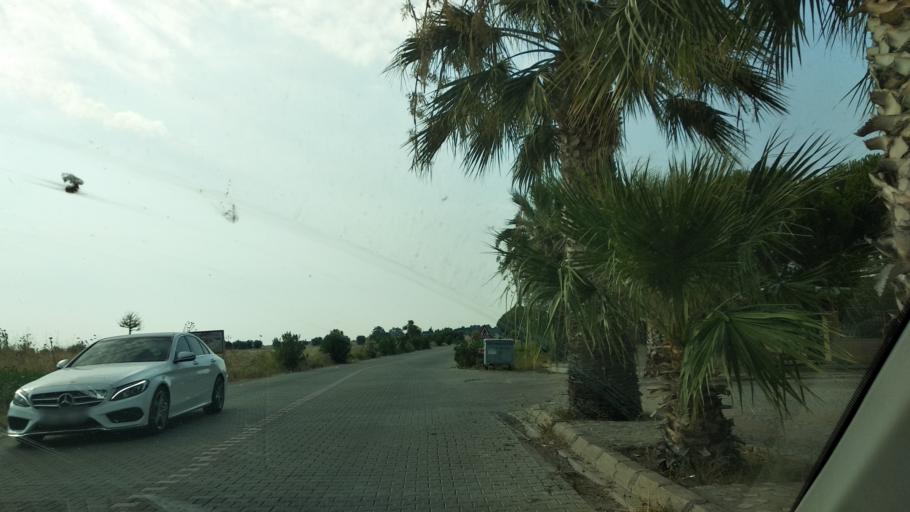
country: TR
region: Izmir
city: Dikili
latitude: 39.1070
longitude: 26.8715
